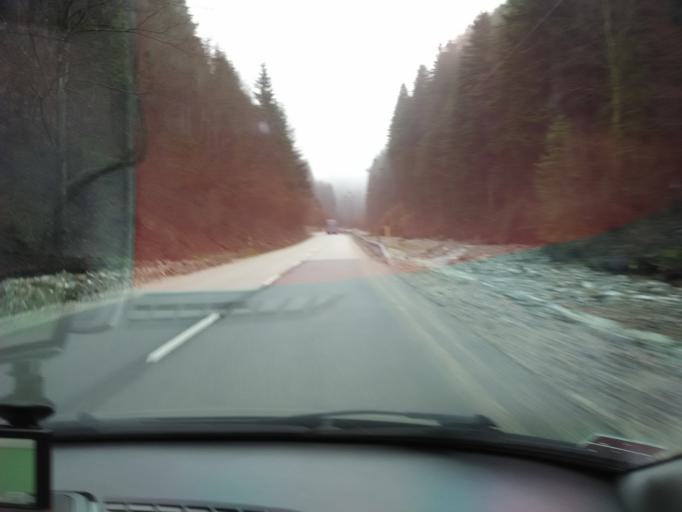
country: SK
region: Zilinsky
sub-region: Okres Zilina
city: Terchova
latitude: 49.2177
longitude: 19.0359
